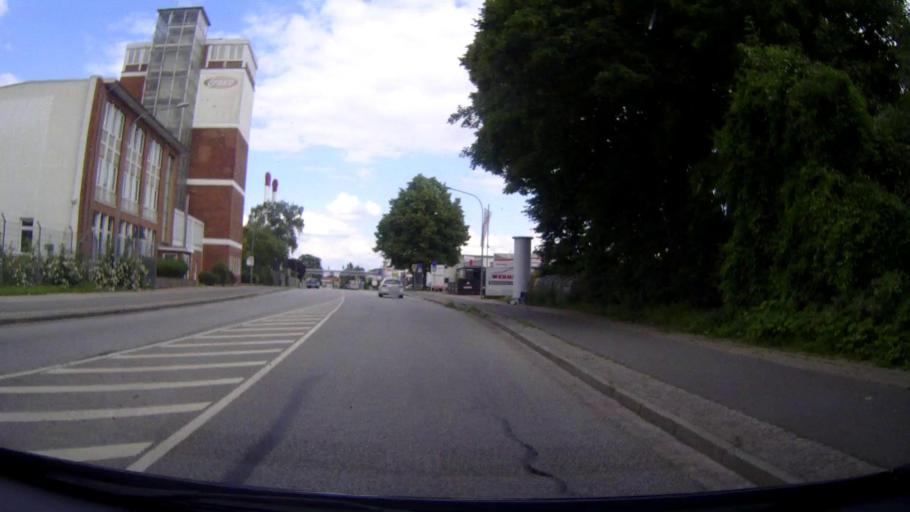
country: DE
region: Schleswig-Holstein
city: Luebeck
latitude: 53.8463
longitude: 10.6667
